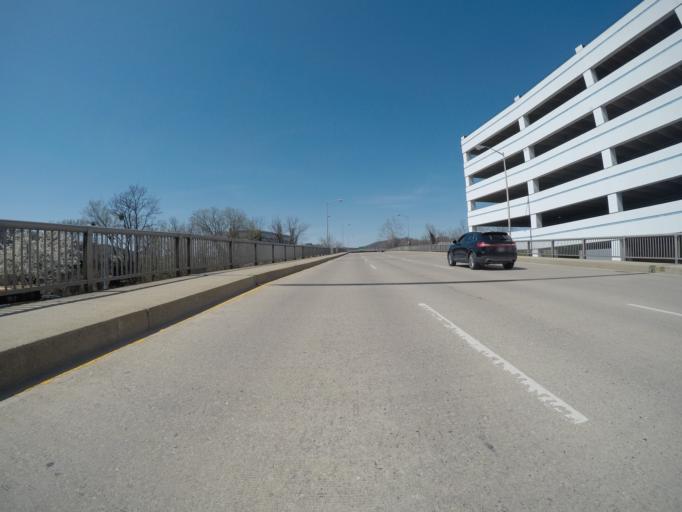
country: US
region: West Virginia
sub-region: Kanawha County
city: Charleston
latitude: 38.3558
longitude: -81.6424
